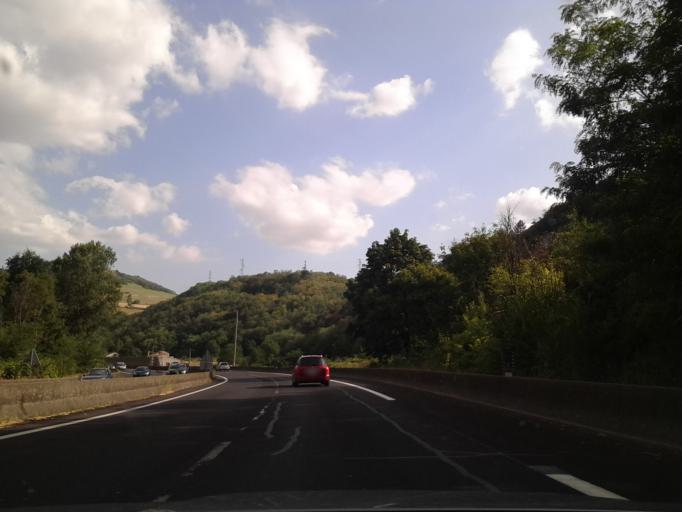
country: FR
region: Auvergne
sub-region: Departement du Puy-de-Dome
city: Vic-le-Comte
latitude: 45.6019
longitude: 3.2168
